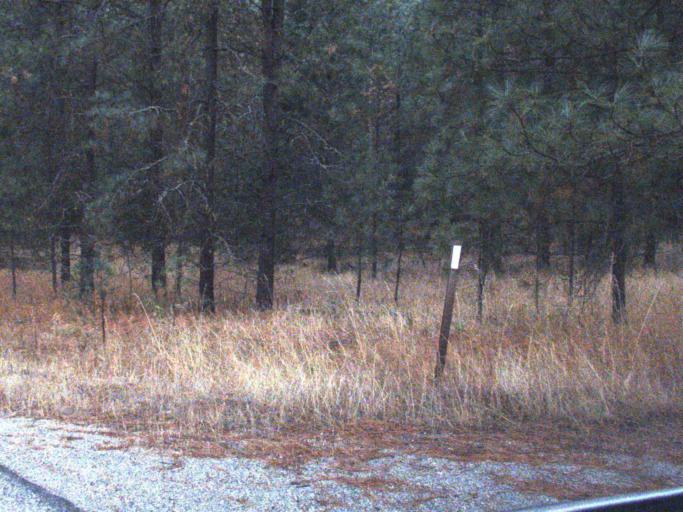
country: CA
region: British Columbia
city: Grand Forks
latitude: 48.9539
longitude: -118.2152
